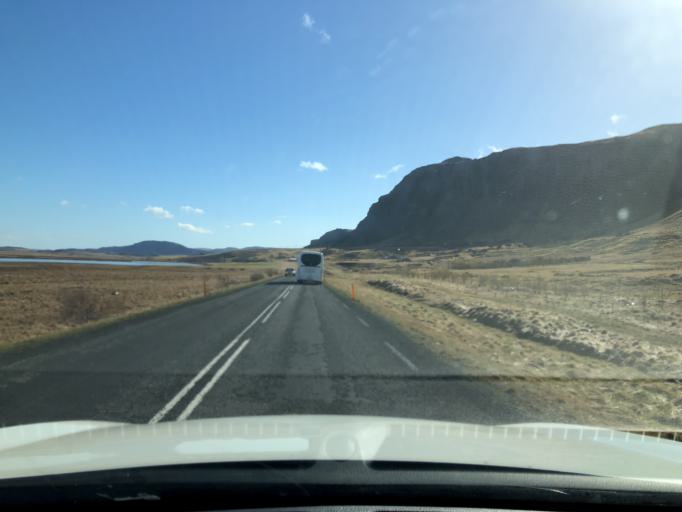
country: IS
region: West
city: Borgarnes
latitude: 64.5316
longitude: -21.7890
